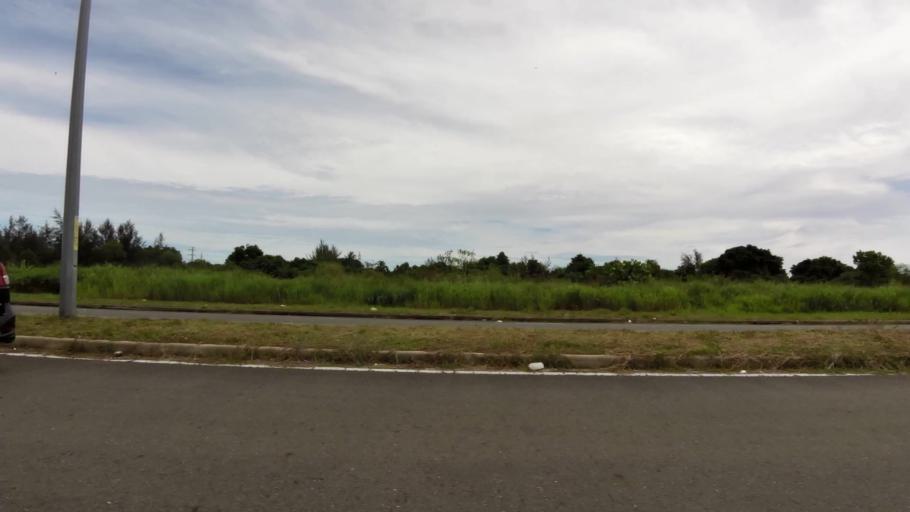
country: BN
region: Belait
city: Kuala Belait
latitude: 4.5892
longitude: 114.2634
